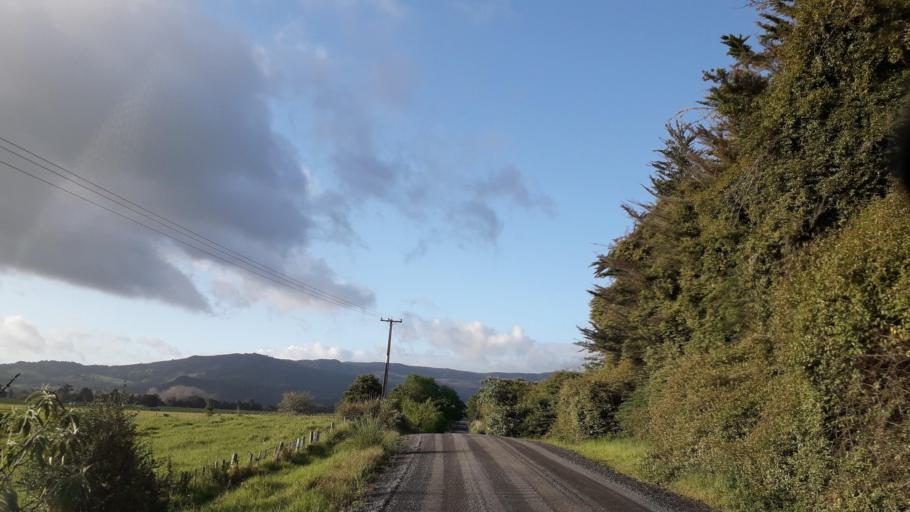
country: NZ
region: Northland
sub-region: Far North District
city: Waimate North
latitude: -35.4931
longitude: 173.6997
